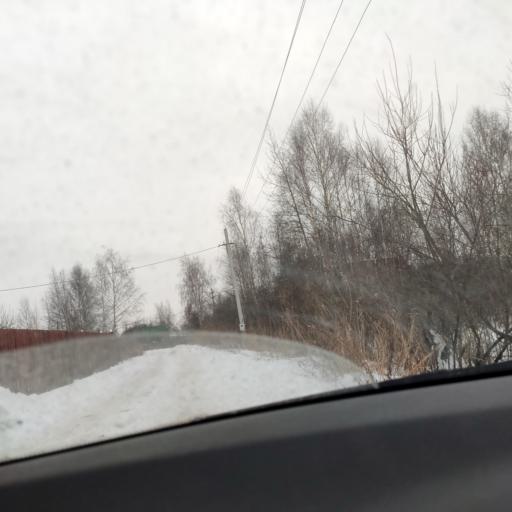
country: RU
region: Perm
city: Kondratovo
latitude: 57.9580
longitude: 56.0872
